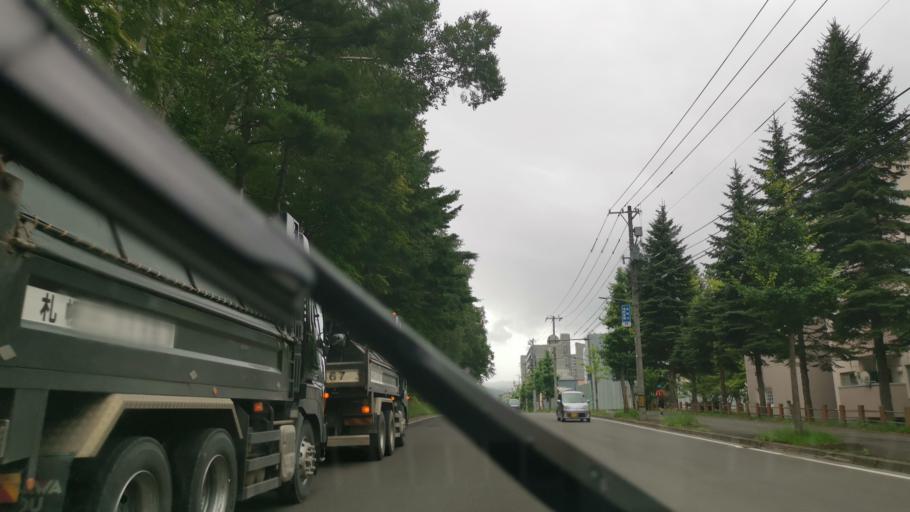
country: JP
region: Hokkaido
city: Sapporo
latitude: 42.9835
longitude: 141.3561
